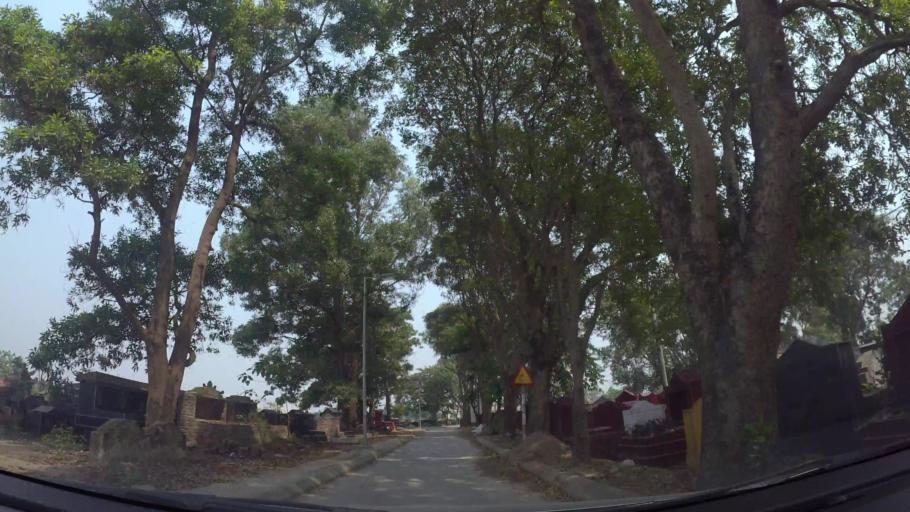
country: VN
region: Ha Noi
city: Ha Dong
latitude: 20.9939
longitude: 105.7660
